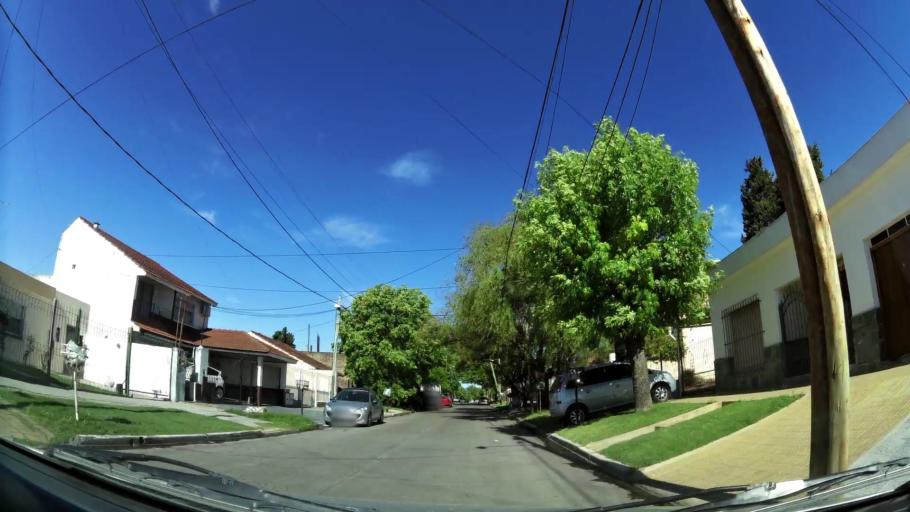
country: AR
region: Buenos Aires
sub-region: Partido de Lomas de Zamora
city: Lomas de Zamora
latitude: -34.7655
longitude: -58.4185
